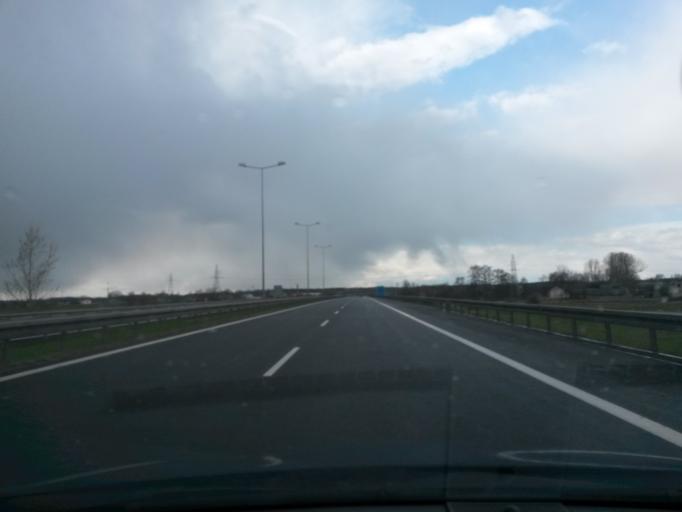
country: PL
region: Greater Poland Voivodeship
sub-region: Powiat koninski
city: Golina
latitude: 52.1806
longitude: 18.1173
